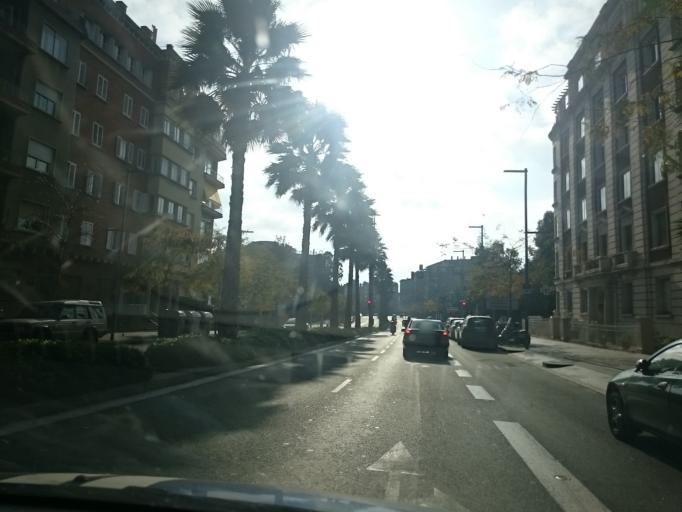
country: ES
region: Catalonia
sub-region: Provincia de Barcelona
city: Sarria-Sant Gervasi
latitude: 41.3999
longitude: 2.1347
